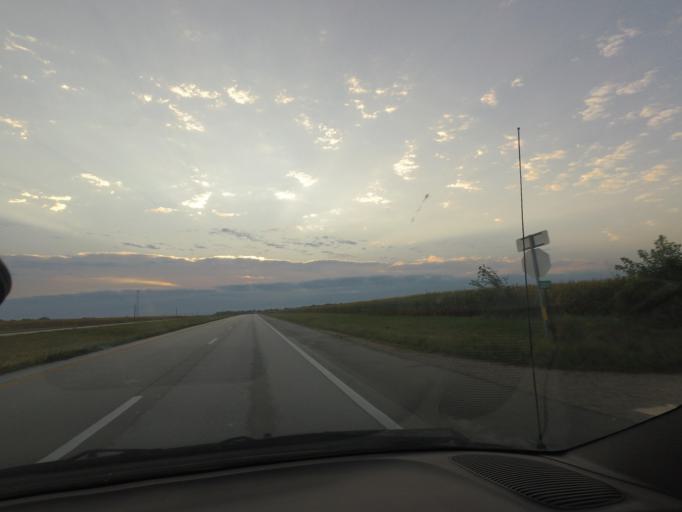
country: US
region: Missouri
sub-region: Macon County
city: Macon
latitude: 39.7503
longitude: -92.2772
